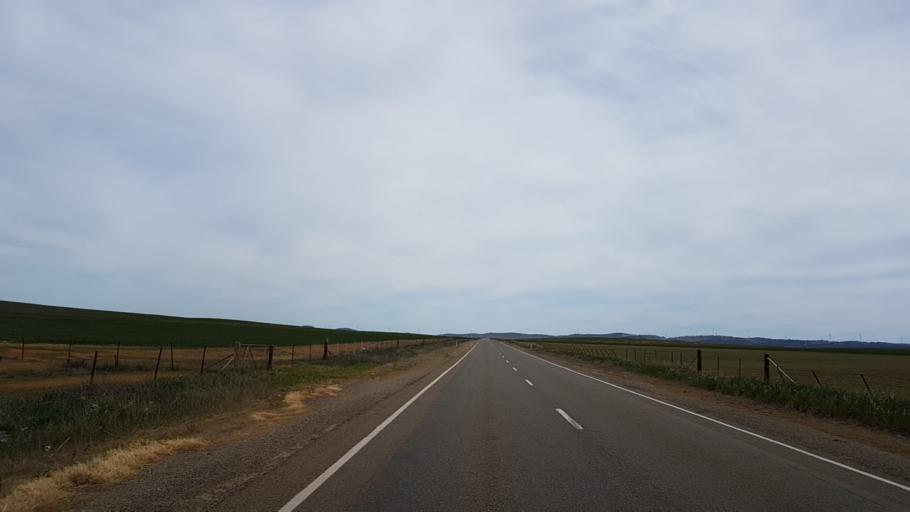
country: AU
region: South Australia
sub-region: Peterborough
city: Peterborough
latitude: -33.0206
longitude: 138.6850
